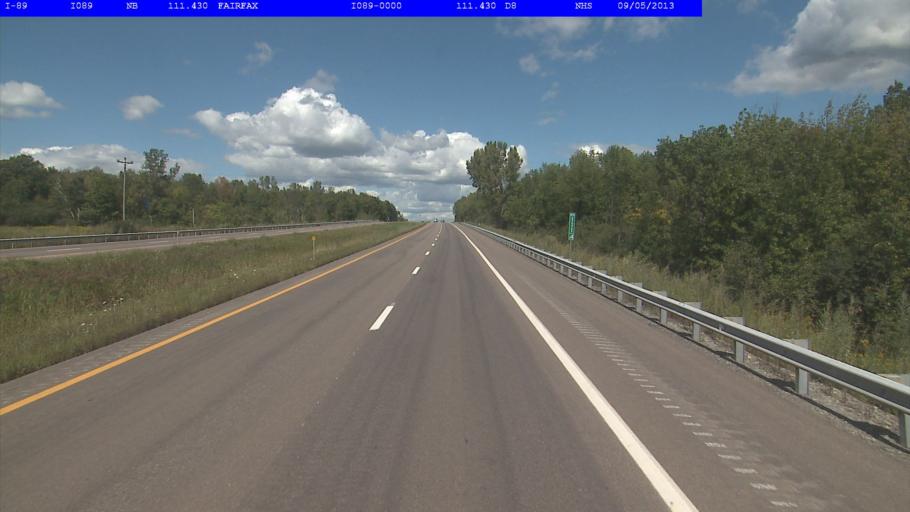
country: US
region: Vermont
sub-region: Franklin County
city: Saint Albans
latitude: 44.7617
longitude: -73.0762
